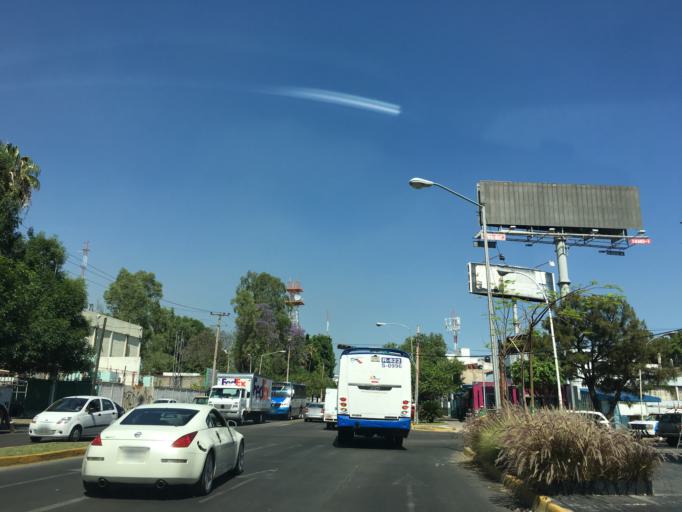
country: MX
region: Jalisco
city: Guadalajara
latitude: 20.6657
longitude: -103.3729
